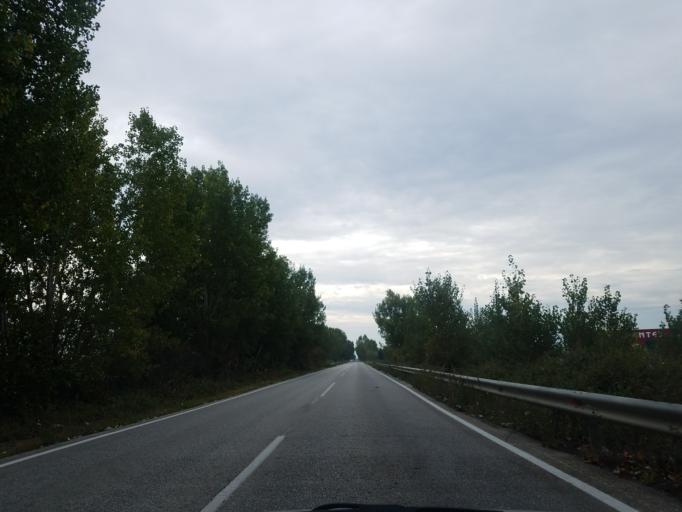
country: GR
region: Thessaly
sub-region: Nomos Kardhitsas
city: Agnantero
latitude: 39.4653
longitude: 21.8522
